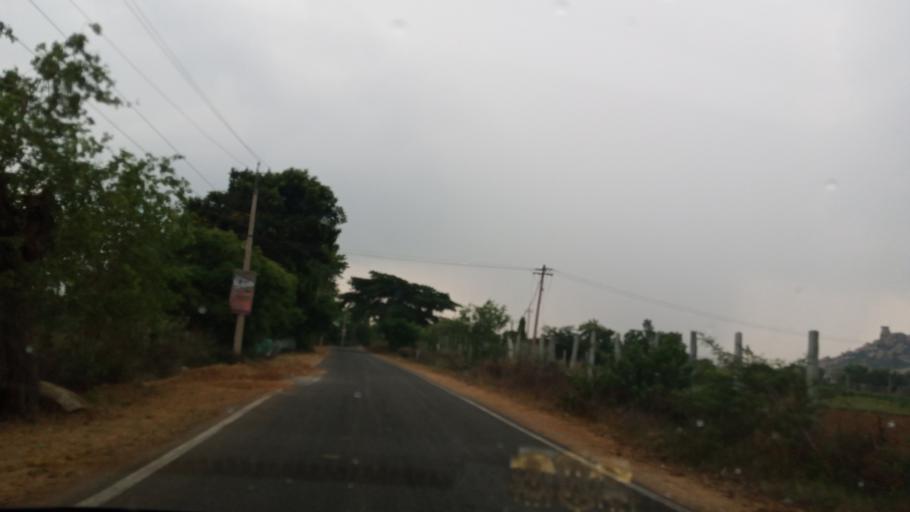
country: IN
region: Karnataka
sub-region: Kolar
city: Mulbagal
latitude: 13.1172
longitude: 78.3368
